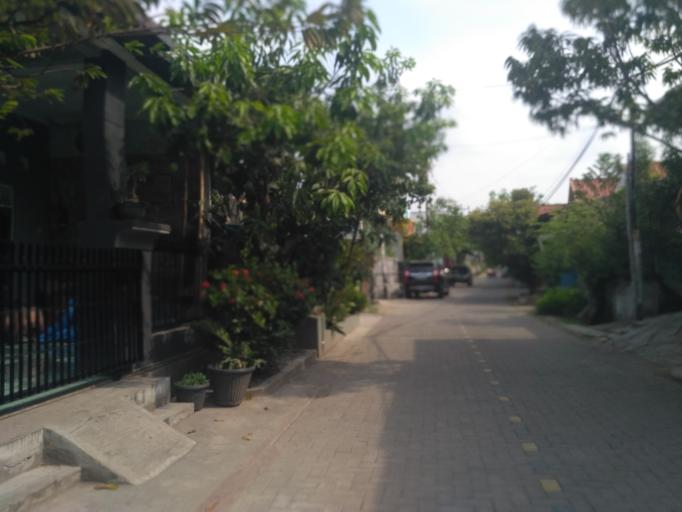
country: ID
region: Central Java
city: Mranggen
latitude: -7.0182
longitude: 110.4822
